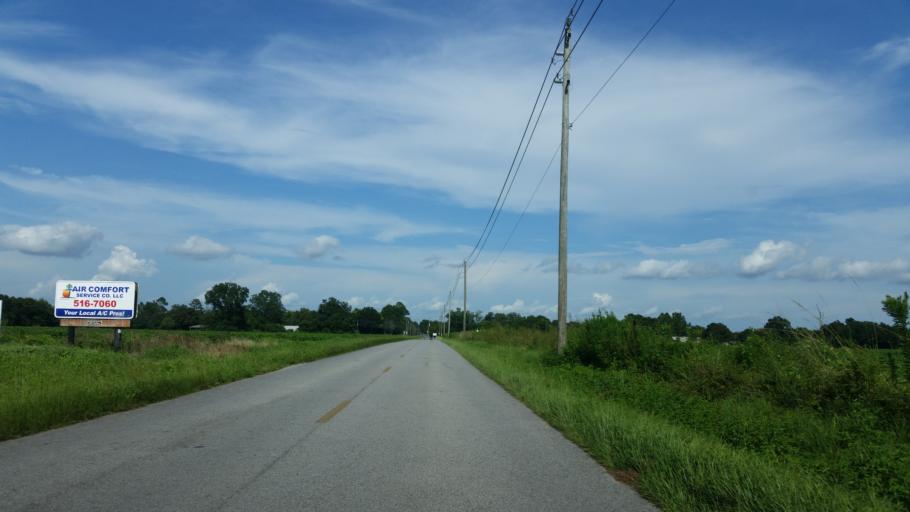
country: US
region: Florida
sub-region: Santa Rosa County
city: Pace
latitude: 30.6184
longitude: -87.1530
